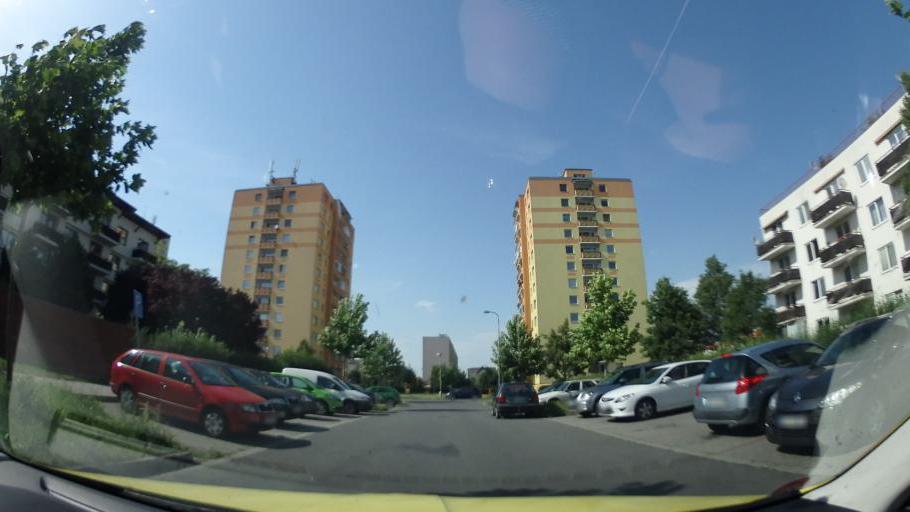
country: CZ
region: Olomoucky
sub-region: Okres Olomouc
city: Olomouc
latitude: 49.5733
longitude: 17.2520
